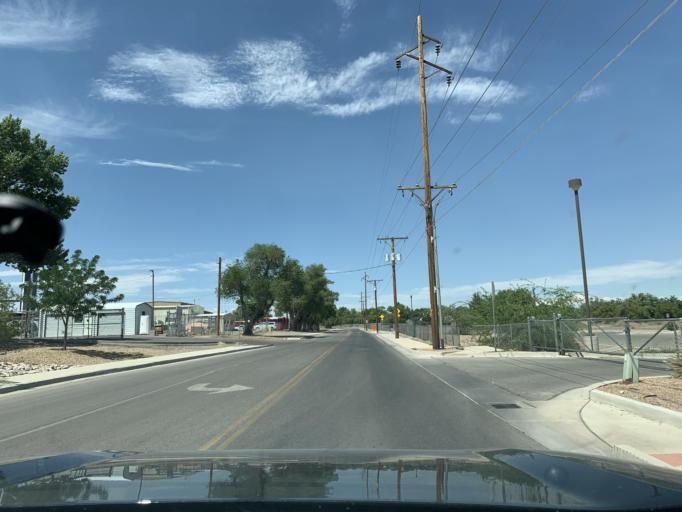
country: US
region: New Mexico
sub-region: Valencia County
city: Los Lunas
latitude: 34.8131
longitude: -106.7398
